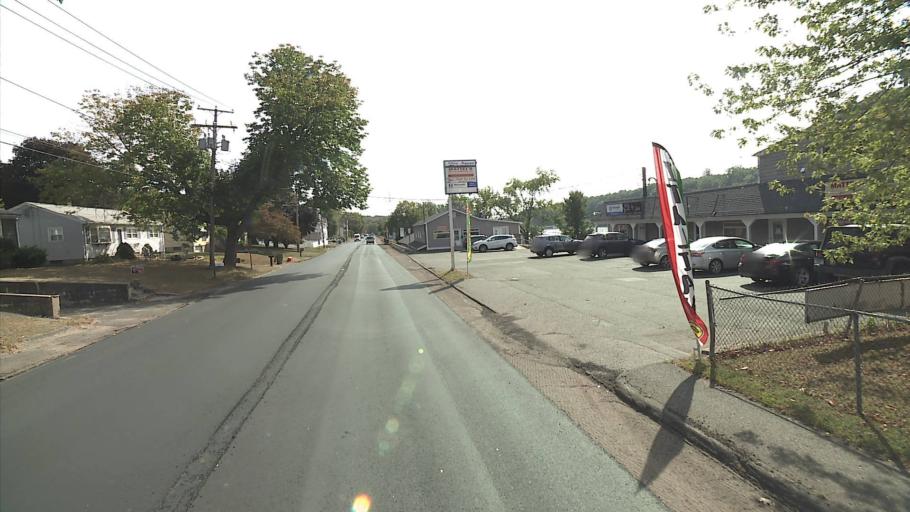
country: US
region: Connecticut
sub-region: Fairfield County
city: Shelton
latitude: 41.3295
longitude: -73.1069
